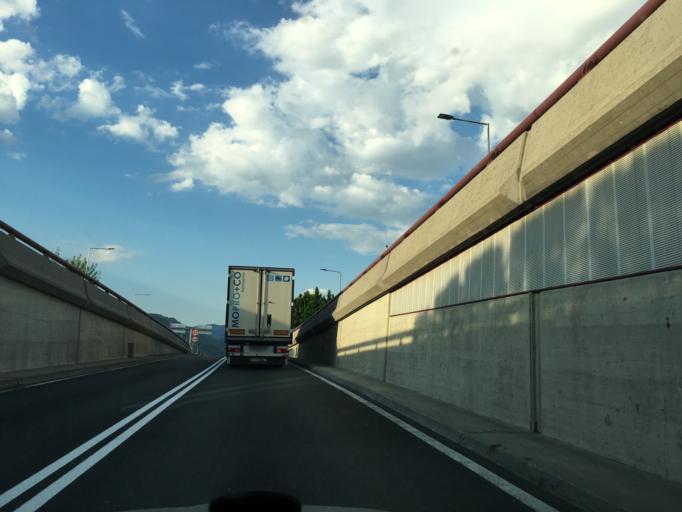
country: AT
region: Tyrol
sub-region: Politischer Bezirk Kitzbuhel
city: Sankt Johann in Tirol
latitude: 47.5245
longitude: 12.4228
